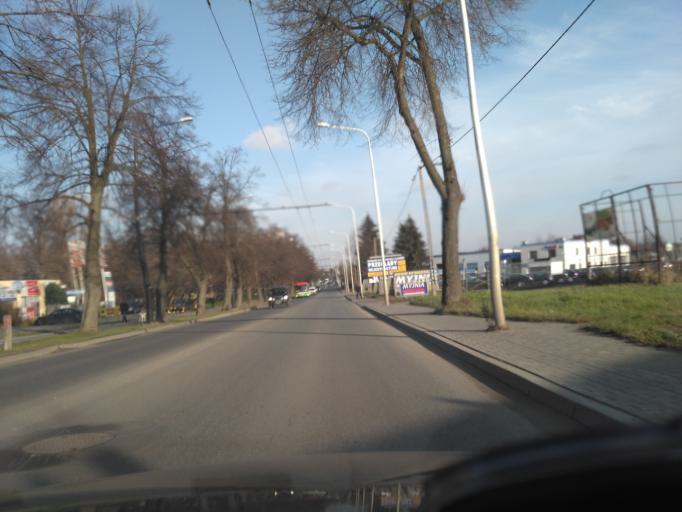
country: PL
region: Lublin Voivodeship
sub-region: Powiat lubelski
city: Lublin
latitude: 51.2093
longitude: 22.5709
